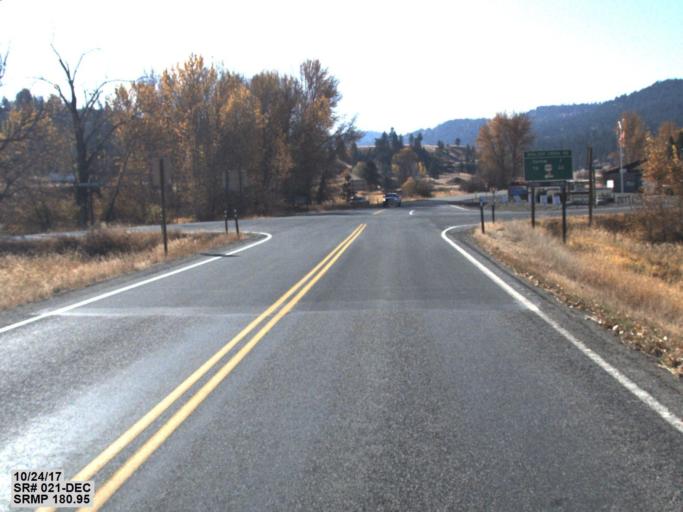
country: CA
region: British Columbia
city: Grand Forks
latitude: 48.8804
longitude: -118.6041
